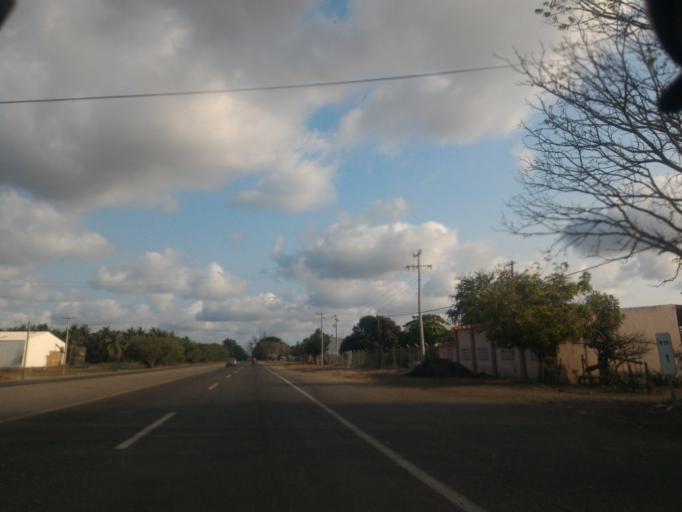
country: MX
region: Colima
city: Tecoman
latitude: 18.8897
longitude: -103.8543
